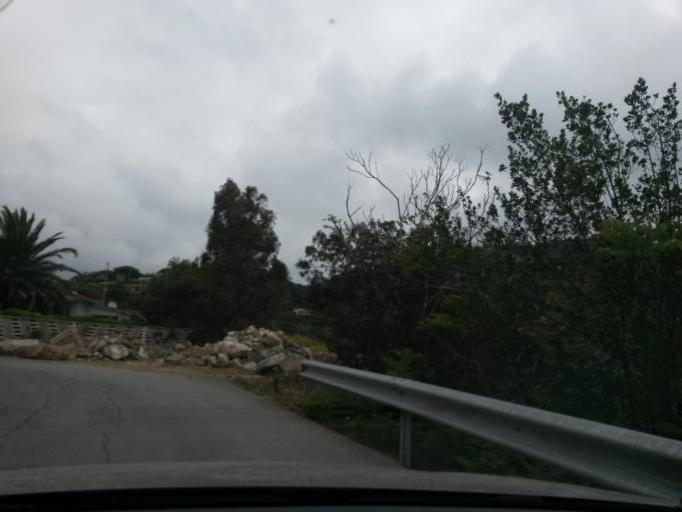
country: IT
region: Tuscany
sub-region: Provincia di Livorno
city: Capoliveri
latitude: 42.7365
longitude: 10.3754
